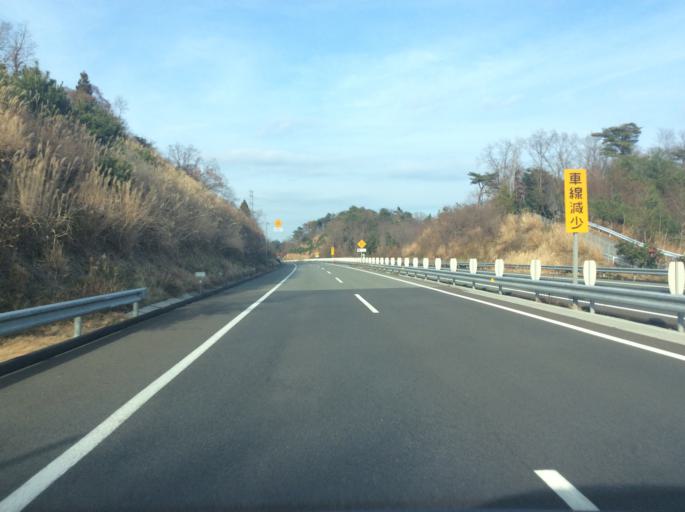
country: JP
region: Fukushima
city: Namie
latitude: 37.3089
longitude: 140.9920
